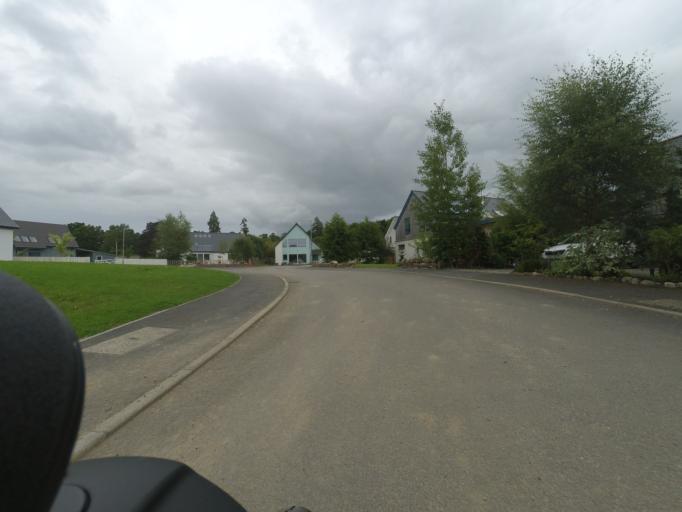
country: GB
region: Scotland
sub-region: Highland
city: Muir of Ord
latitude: 57.5703
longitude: -4.5766
